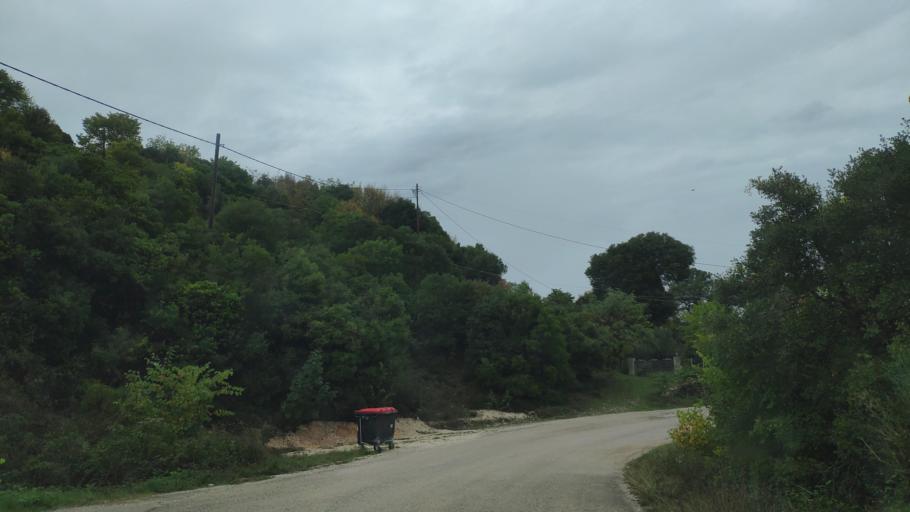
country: GR
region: Epirus
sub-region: Nomos Thesprotias
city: Paramythia
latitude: 39.4644
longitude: 20.6722
